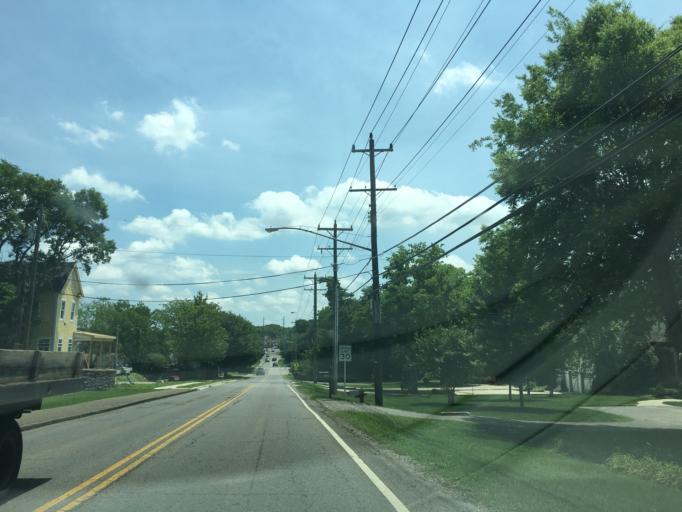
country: US
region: Tennessee
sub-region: Davidson County
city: Belle Meade
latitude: 36.1014
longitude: -86.8239
